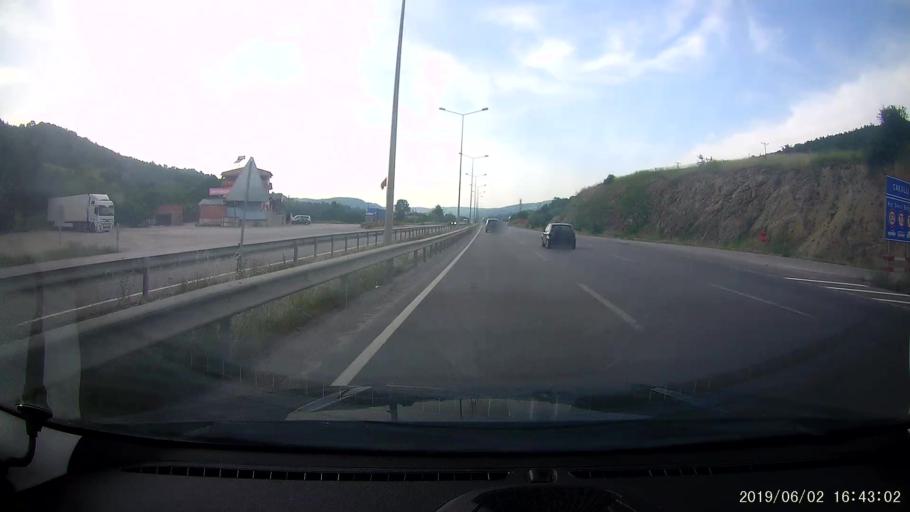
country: TR
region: Samsun
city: Kavak
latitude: 41.1287
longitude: 36.1350
